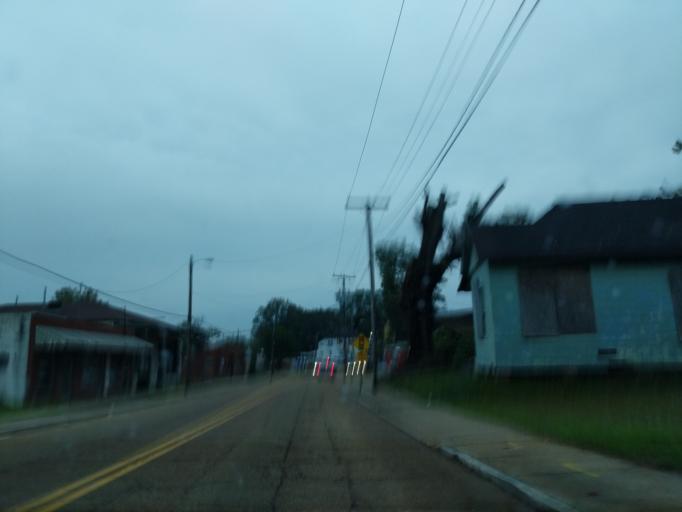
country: US
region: Mississippi
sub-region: Warren County
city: Vicksburg
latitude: 32.3376
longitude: -90.8864
